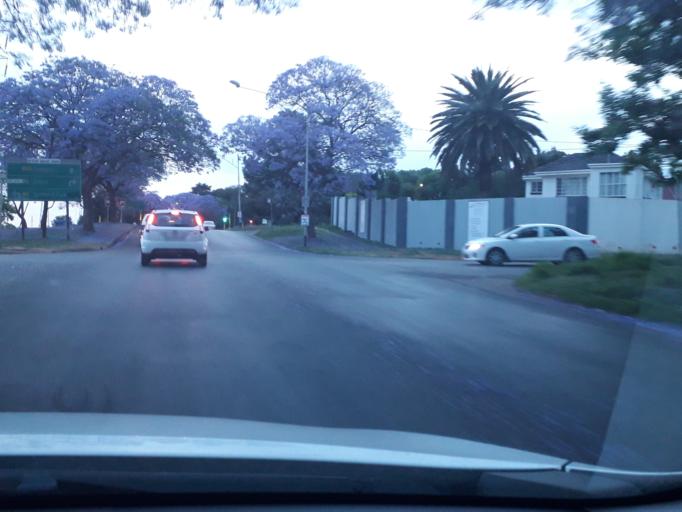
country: ZA
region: Gauteng
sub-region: City of Johannesburg Metropolitan Municipality
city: Johannesburg
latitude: -26.1505
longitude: 27.9896
